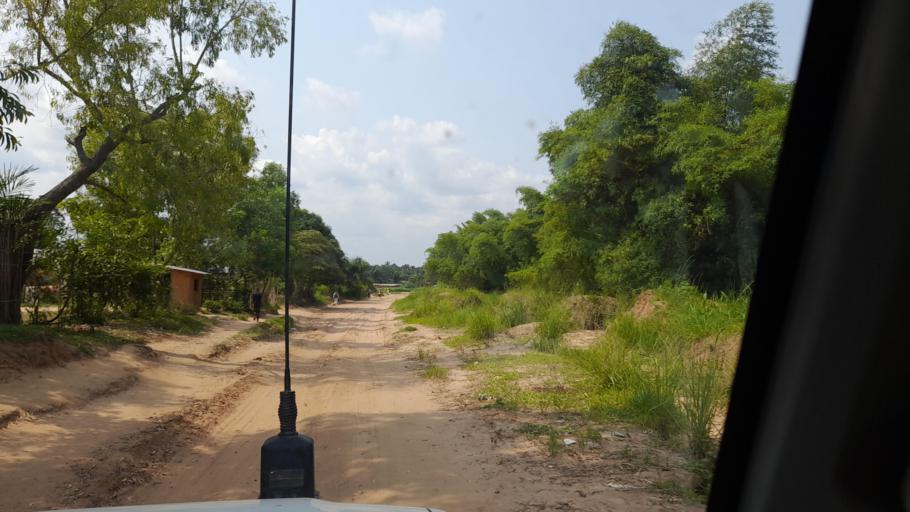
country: CD
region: Kasai-Occidental
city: Kananga
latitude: -5.9107
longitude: 22.4758
